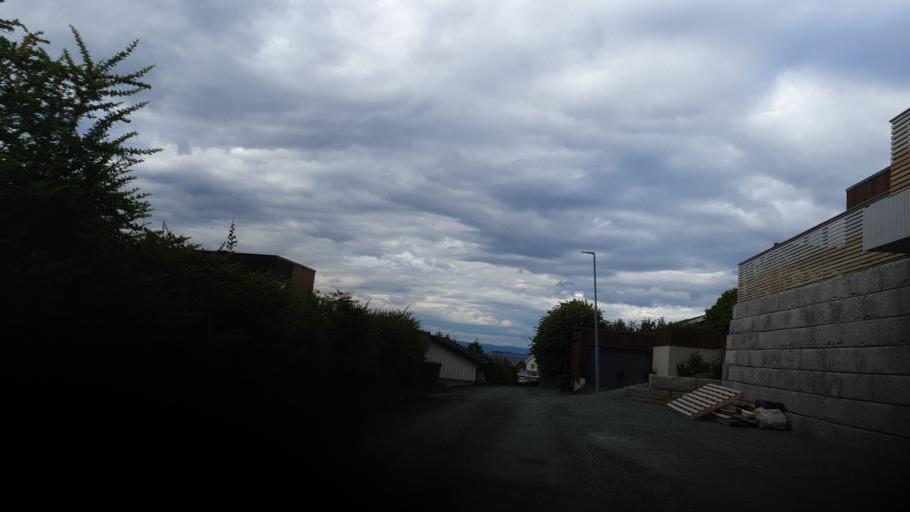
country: NO
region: Sor-Trondelag
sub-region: Klaebu
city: Klaebu
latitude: 63.4267
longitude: 10.5394
